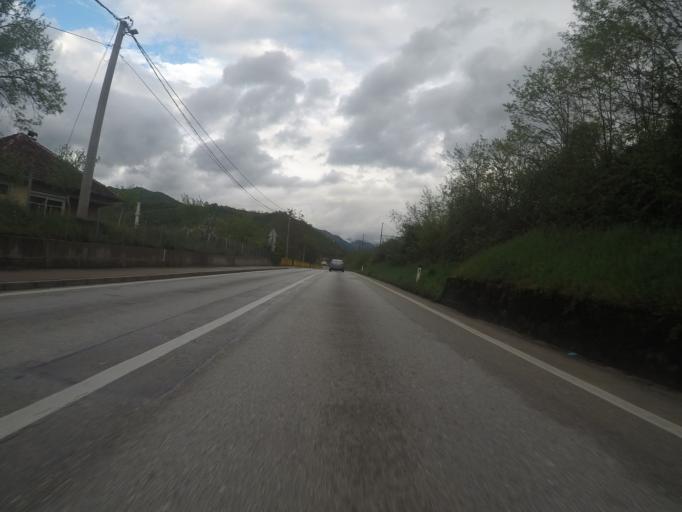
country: BA
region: Federation of Bosnia and Herzegovina
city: Konjic
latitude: 43.6834
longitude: 17.8996
